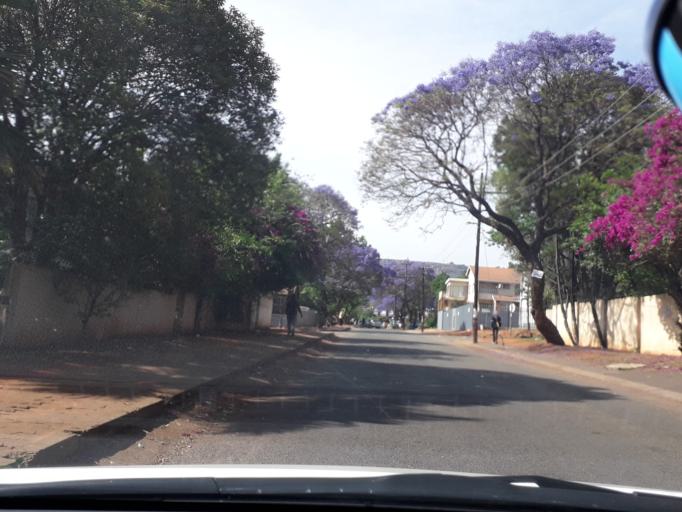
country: ZA
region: Gauteng
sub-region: City of Johannesburg Metropolitan Municipality
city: Roodepoort
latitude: -26.1233
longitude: 27.9660
